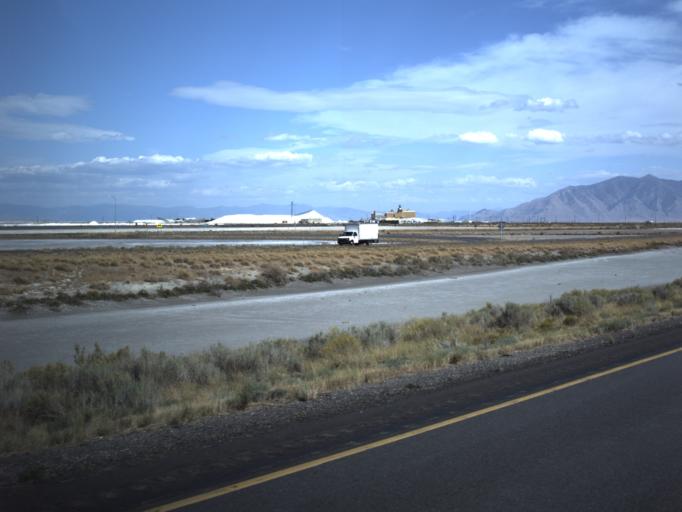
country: US
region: Utah
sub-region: Tooele County
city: Grantsville
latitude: 40.7079
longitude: -112.5264
